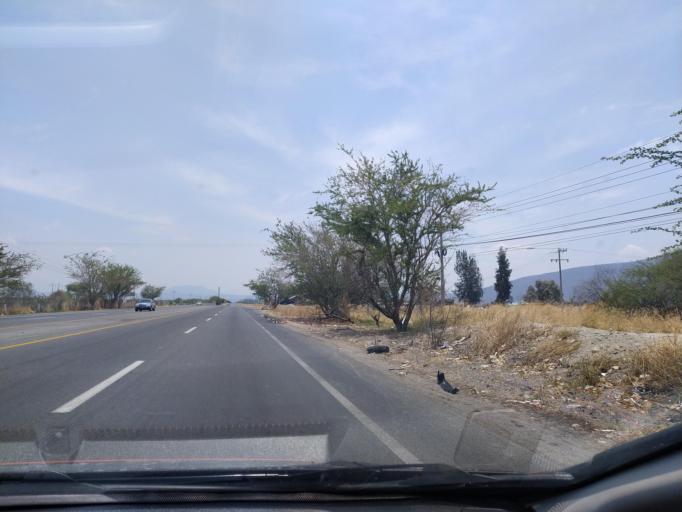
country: MX
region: Jalisco
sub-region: Acatlan de Juarez
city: Villa de los Ninos
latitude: 20.3477
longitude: -103.5914
